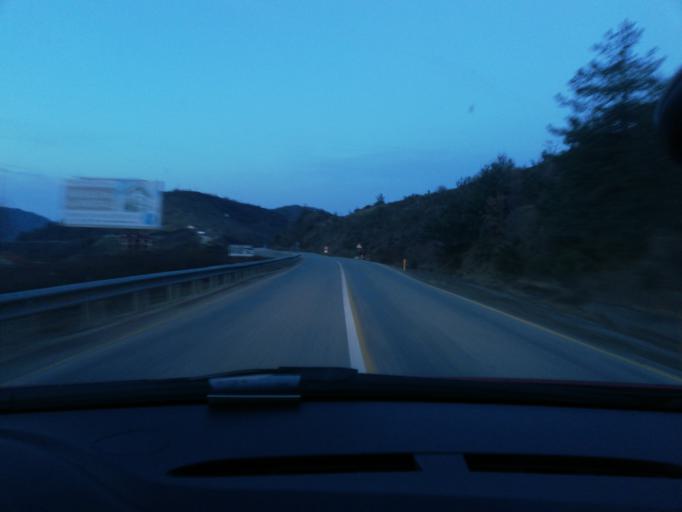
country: TR
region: Kastamonu
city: Inebolu
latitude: 41.9275
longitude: 33.7416
